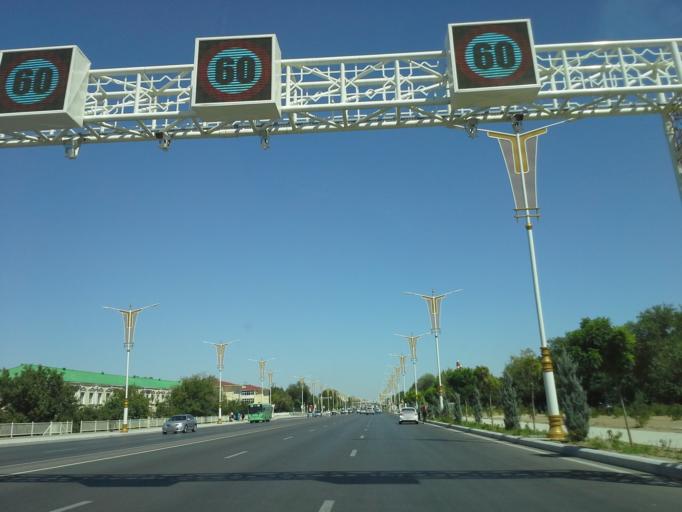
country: TM
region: Ahal
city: Ashgabat
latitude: 37.9101
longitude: 58.4089
